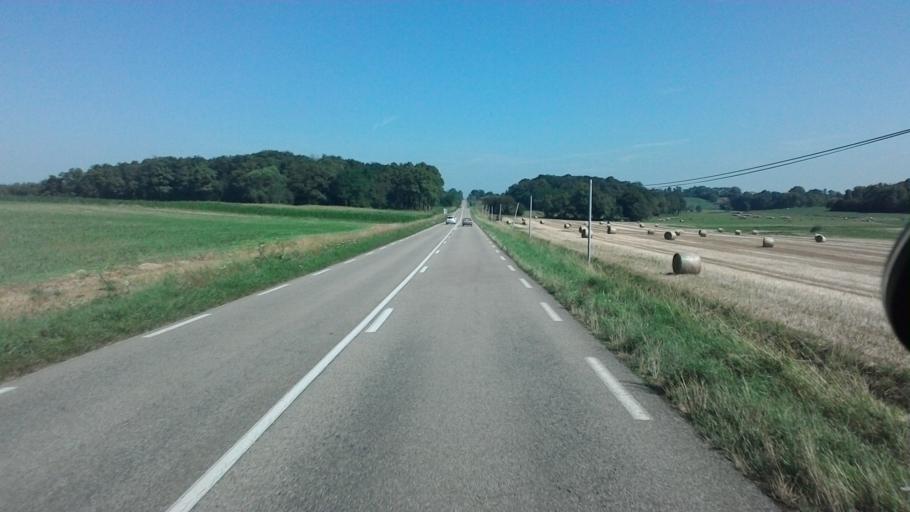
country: FR
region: Rhone-Alpes
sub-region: Departement de l'Ain
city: Saint-Trivier-de-Courtes
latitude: 46.4745
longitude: 5.0747
